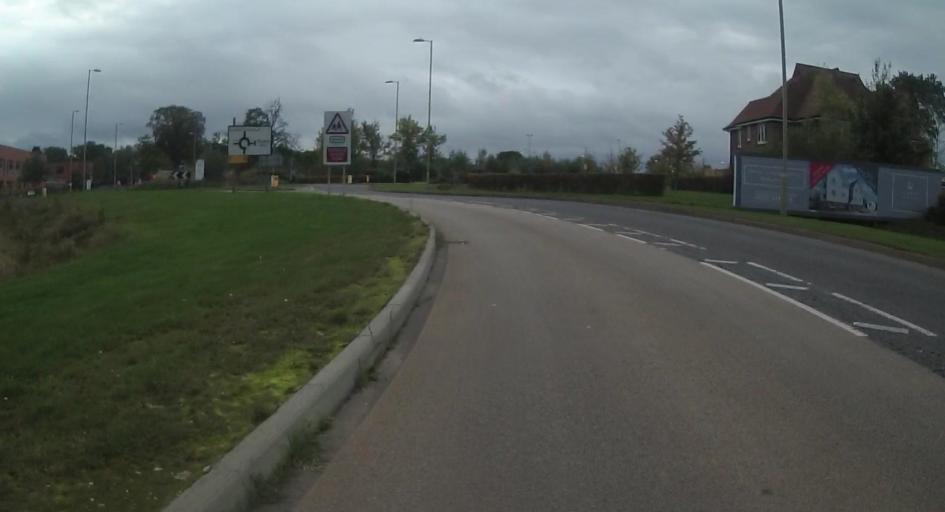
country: GB
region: England
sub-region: Hampshire
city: Fleet
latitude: 51.2802
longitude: -0.8633
